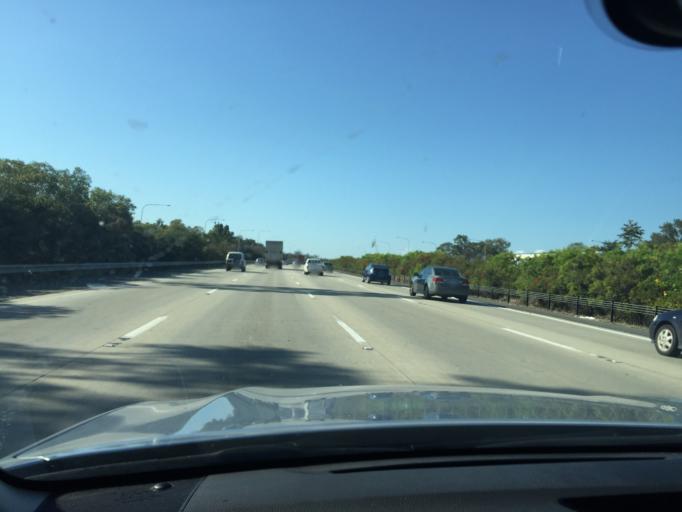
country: AU
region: Queensland
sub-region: Gold Coast
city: Yatala
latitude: -27.7356
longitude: 153.2285
